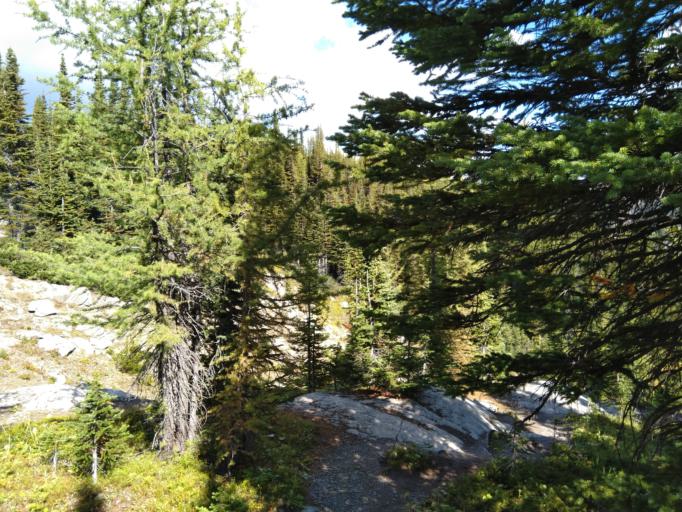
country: CA
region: Alberta
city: Banff
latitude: 51.0844
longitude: -115.7883
